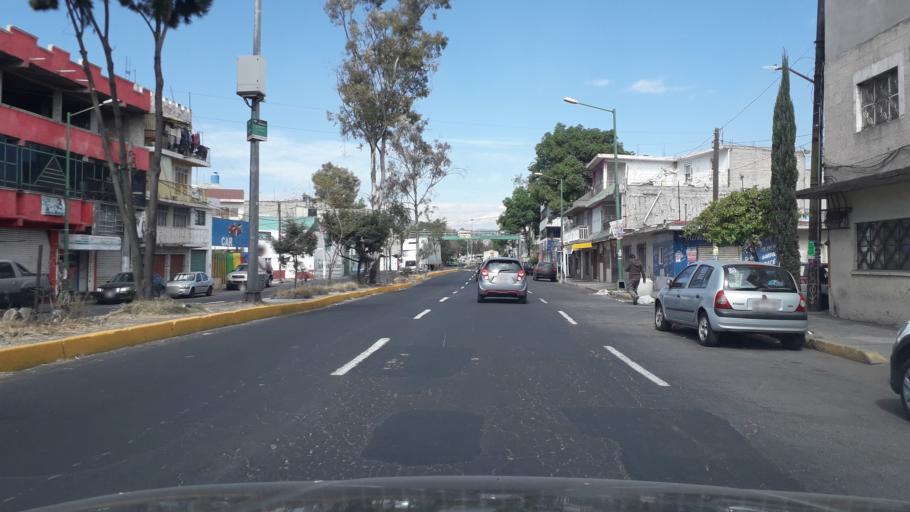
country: MX
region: Mexico City
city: Gustavo A. Madero
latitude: 19.5030
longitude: -99.0903
